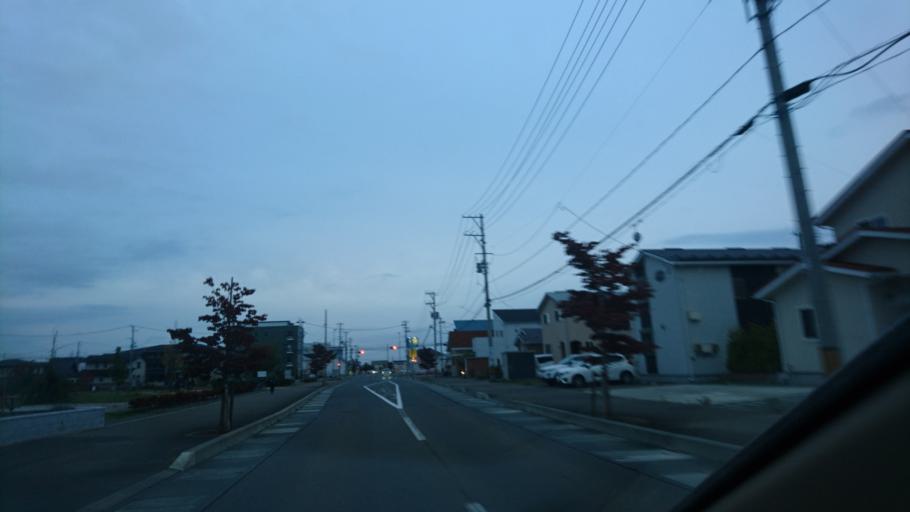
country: JP
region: Iwate
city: Morioka-shi
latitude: 39.6738
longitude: 141.1321
